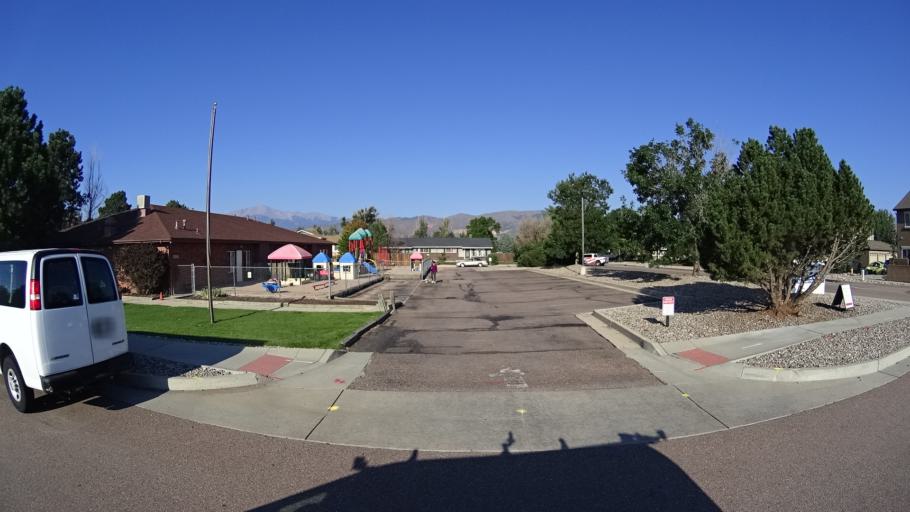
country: US
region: Colorado
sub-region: El Paso County
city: Air Force Academy
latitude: 38.9296
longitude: -104.7967
